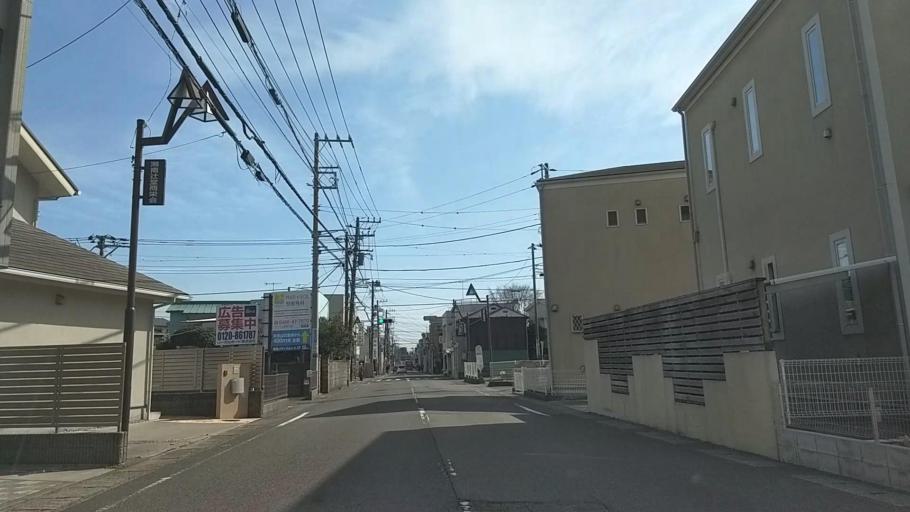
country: JP
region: Kanagawa
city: Fujisawa
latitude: 35.3324
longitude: 139.4507
